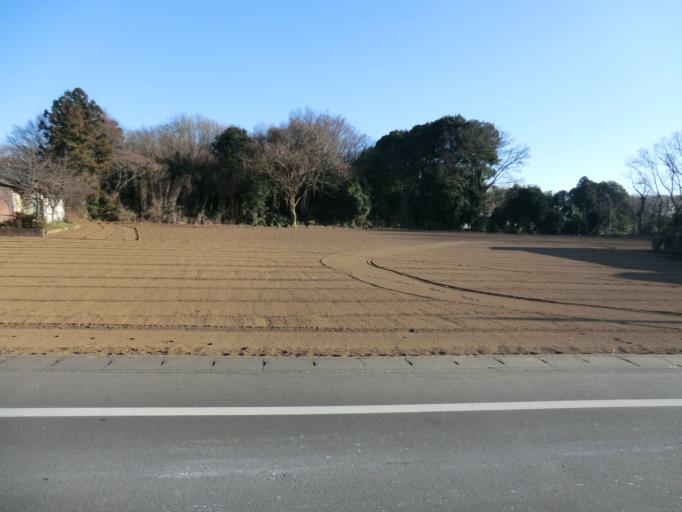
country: JP
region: Ibaraki
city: Mitsukaido
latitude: 35.9711
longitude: 139.9504
